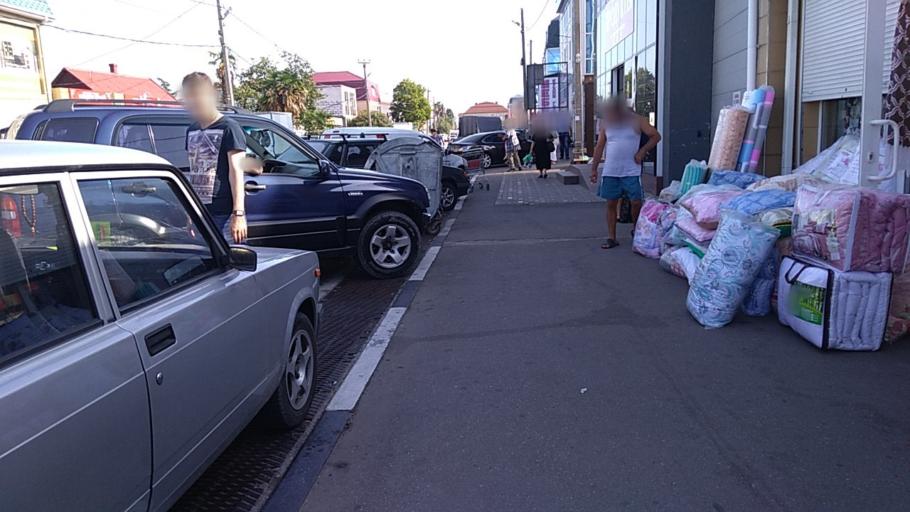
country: RU
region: Krasnodarskiy
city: Vysokoye
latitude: 43.3992
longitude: 40.0033
